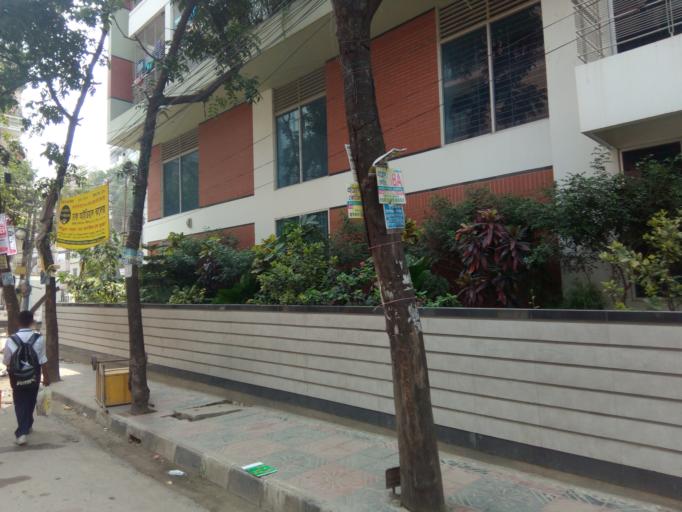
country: BD
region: Dhaka
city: Paltan
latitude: 23.7526
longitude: 90.4172
